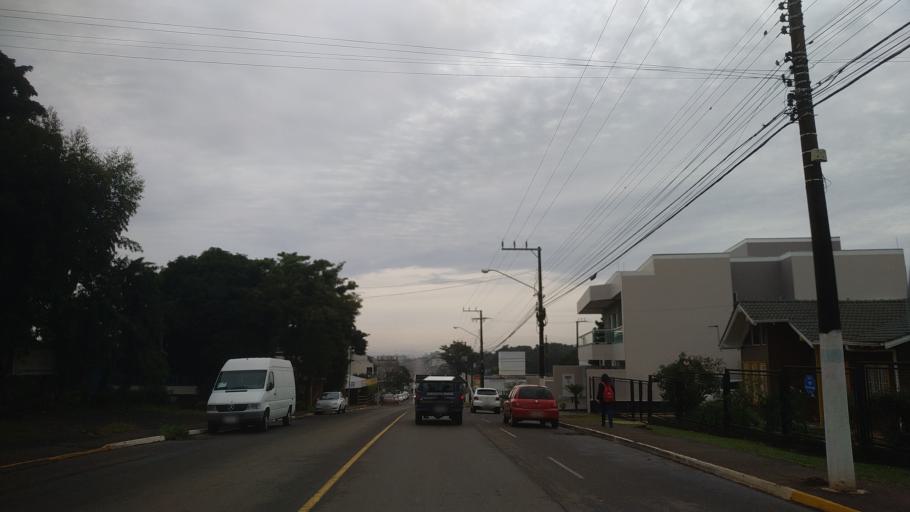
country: BR
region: Santa Catarina
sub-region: Chapeco
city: Chapeco
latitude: -27.0994
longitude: -52.6738
